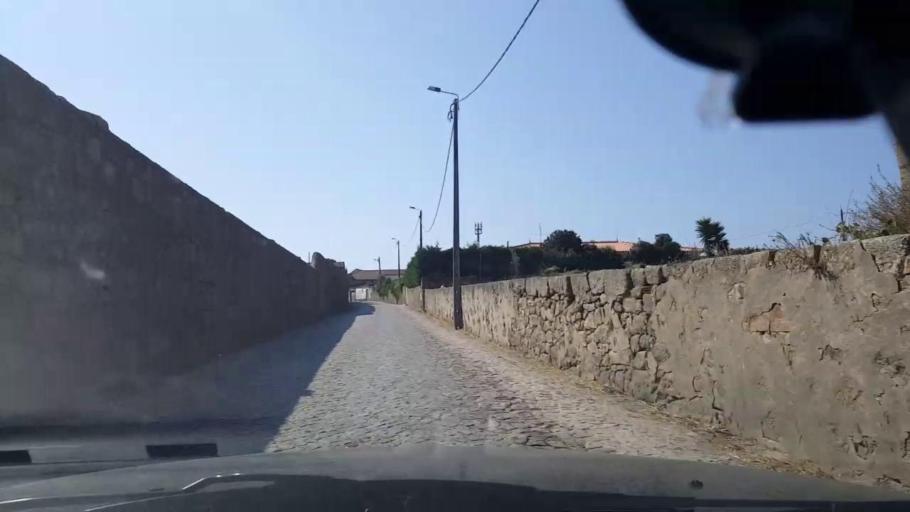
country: PT
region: Porto
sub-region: Vila do Conde
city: Vila do Conde
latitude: 41.3748
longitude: -8.7143
